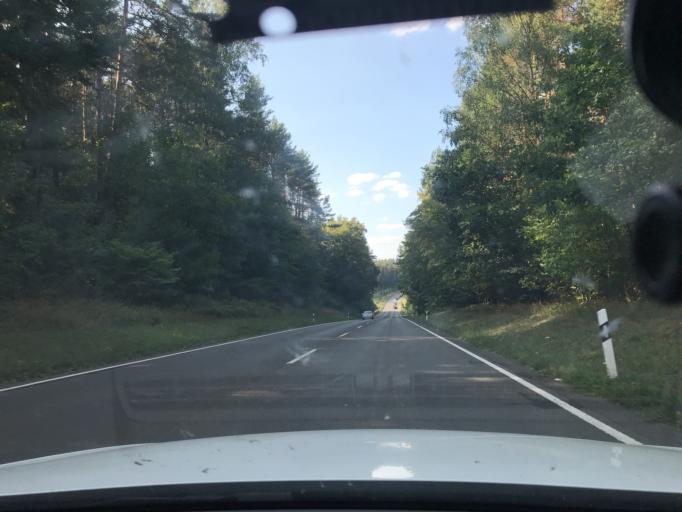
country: DE
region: Bavaria
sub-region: Upper Palatinate
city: Sulzbach-Rosenberg
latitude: 49.4808
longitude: 11.7345
